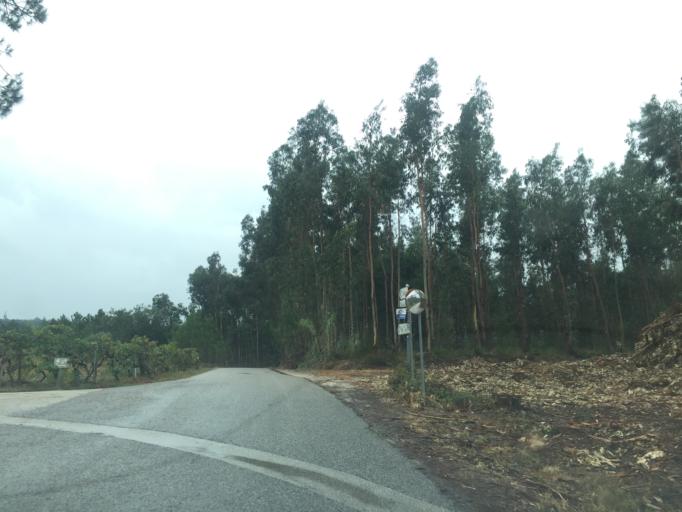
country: PT
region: Leiria
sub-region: Pombal
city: Lourical
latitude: 40.0531
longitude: -8.7760
